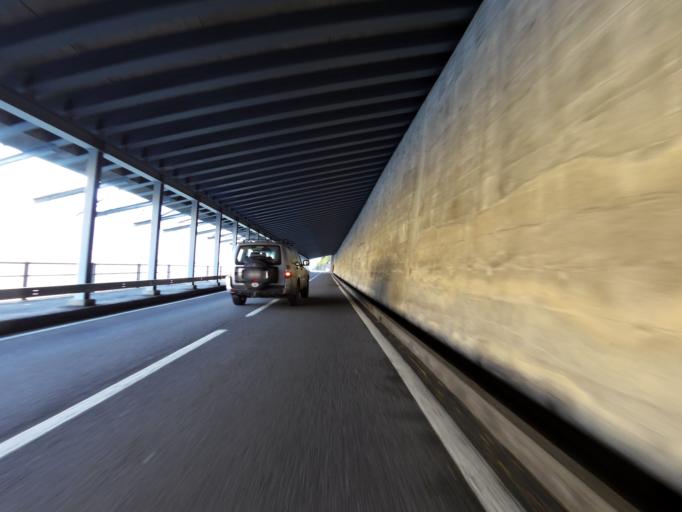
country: CH
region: Uri
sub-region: Uri
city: Bauen
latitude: 46.9124
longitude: 8.5921
